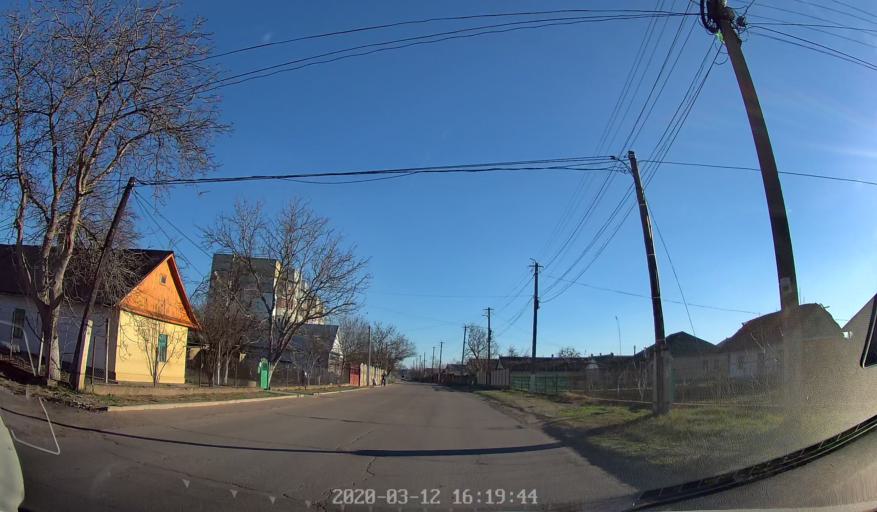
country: MD
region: Anenii Noi
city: Anenii Noi
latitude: 46.8824
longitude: 29.3054
